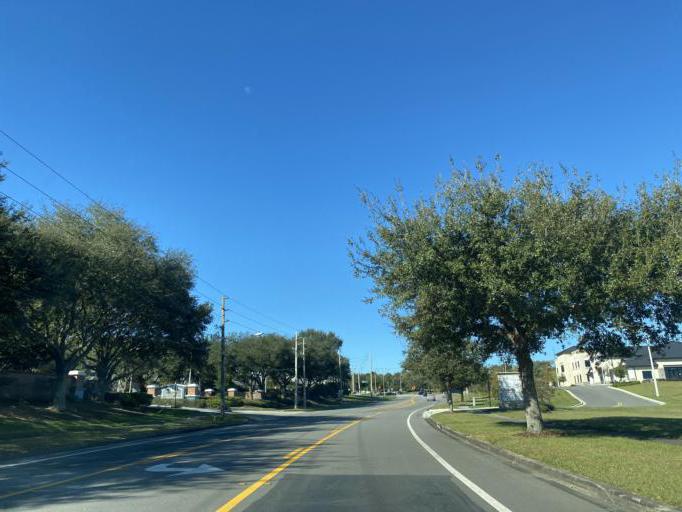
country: US
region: Florida
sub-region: Lake County
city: Clermont
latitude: 28.5267
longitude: -81.7269
